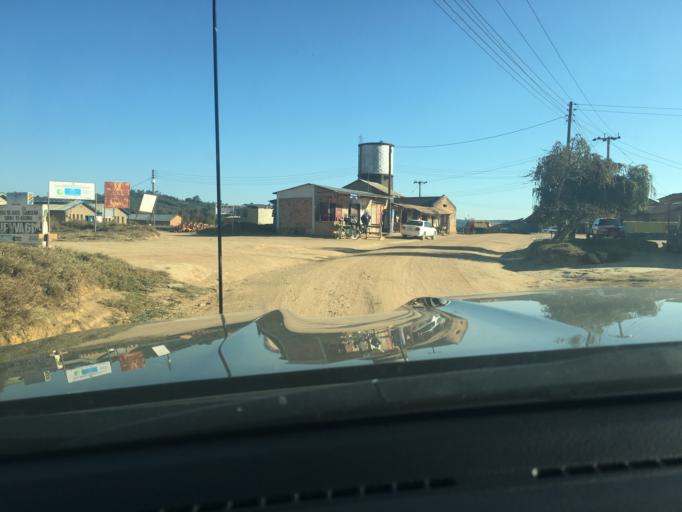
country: TZ
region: Iringa
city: Makungu
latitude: -8.4180
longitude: 35.4202
